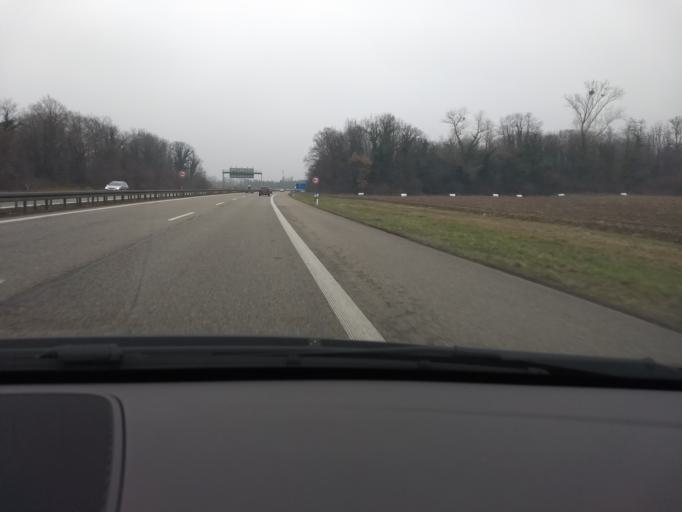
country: FR
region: Alsace
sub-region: Departement du Haut-Rhin
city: Kembs
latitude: 47.6650
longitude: 7.5256
